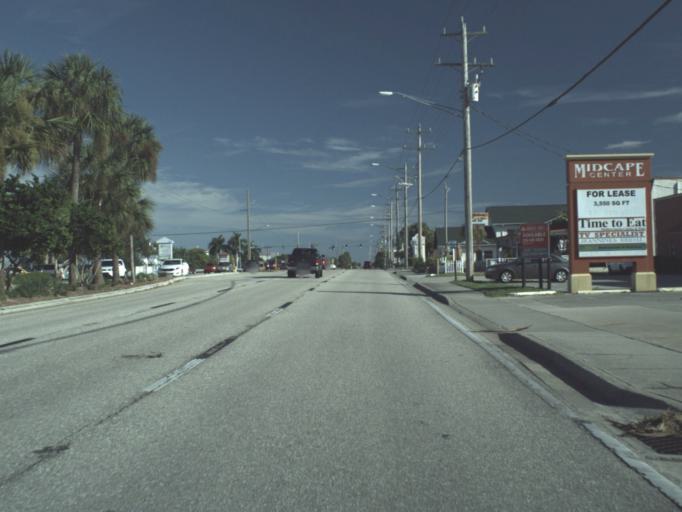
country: US
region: Florida
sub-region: Lee County
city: Lochmoor Waterway Estates
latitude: 26.6274
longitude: -81.9407
